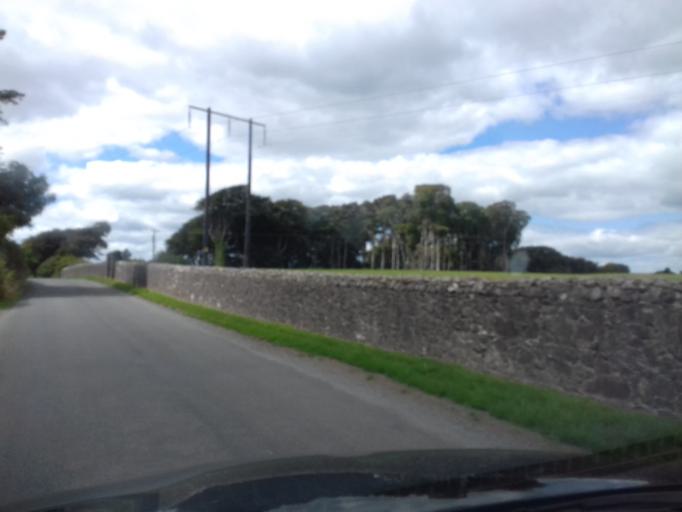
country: IE
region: Munster
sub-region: Waterford
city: Portlaw
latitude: 52.1774
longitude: -7.3567
